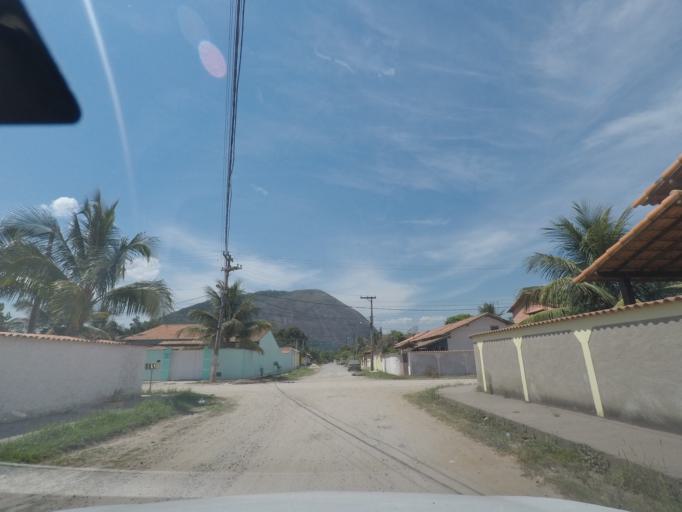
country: BR
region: Rio de Janeiro
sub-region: Marica
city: Marica
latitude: -22.9547
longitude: -42.9604
